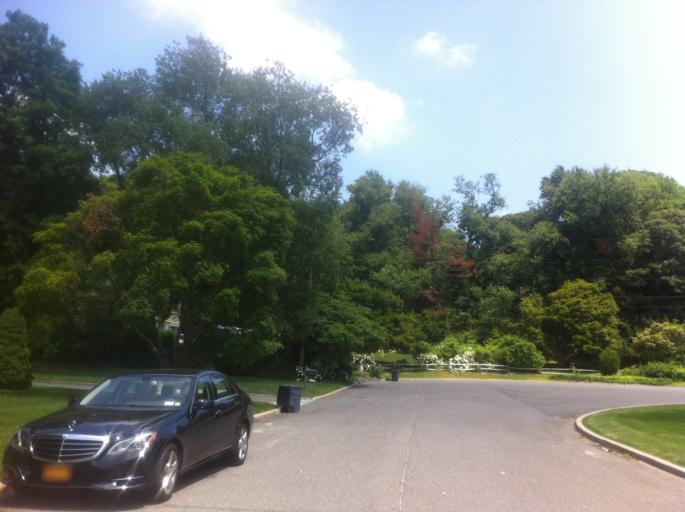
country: US
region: New York
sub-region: Nassau County
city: Locust Valley
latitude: 40.8577
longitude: -73.5994
